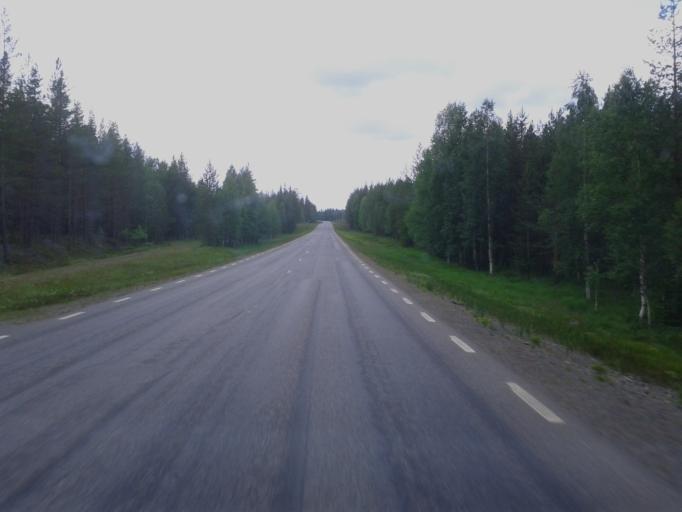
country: SE
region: Vaesterbotten
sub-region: Mala Kommun
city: Mala
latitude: 65.2179
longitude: 18.6581
